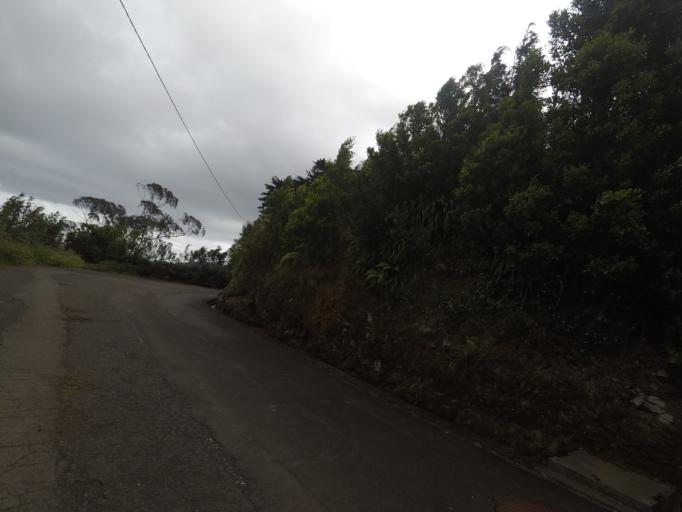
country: PT
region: Madeira
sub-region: Santa Cruz
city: Santa Cruz
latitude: 32.7474
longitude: -16.8255
